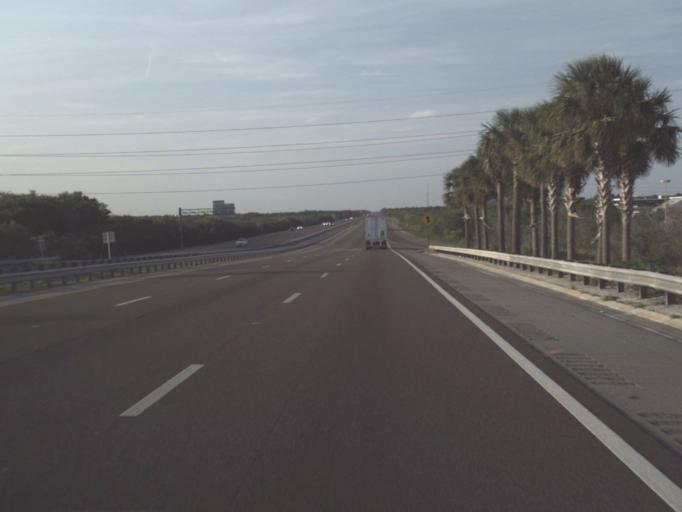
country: US
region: Florida
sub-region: Brevard County
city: Titusville
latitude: 28.5532
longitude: -80.8514
